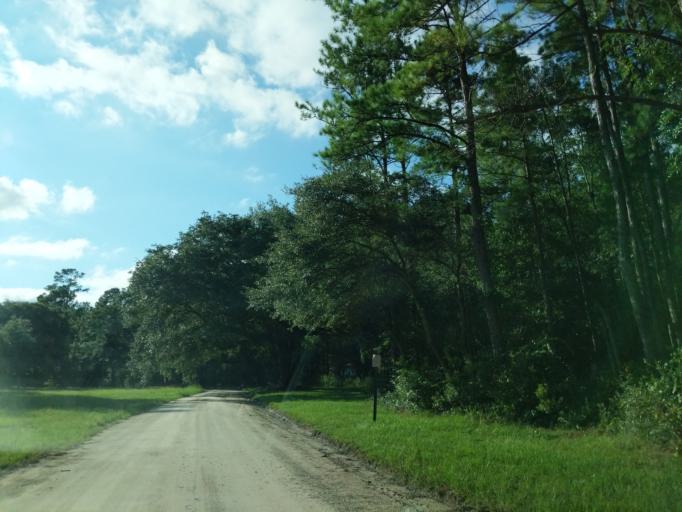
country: US
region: South Carolina
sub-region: Charleston County
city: Awendaw
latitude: 33.1514
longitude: -79.4094
